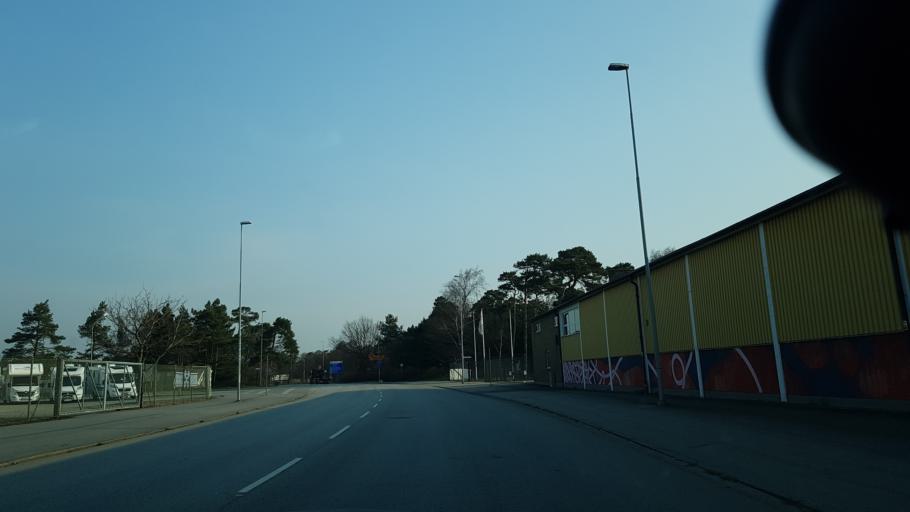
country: SE
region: Skane
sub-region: Ystads Kommun
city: Ystad
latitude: 55.4270
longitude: 13.8407
